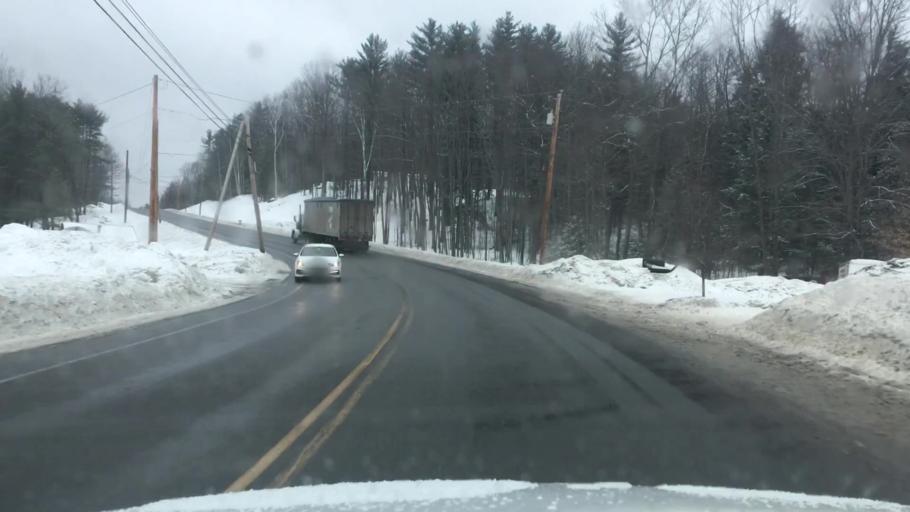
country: US
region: Maine
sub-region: Oxford County
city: Peru
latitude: 44.5190
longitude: -70.4082
